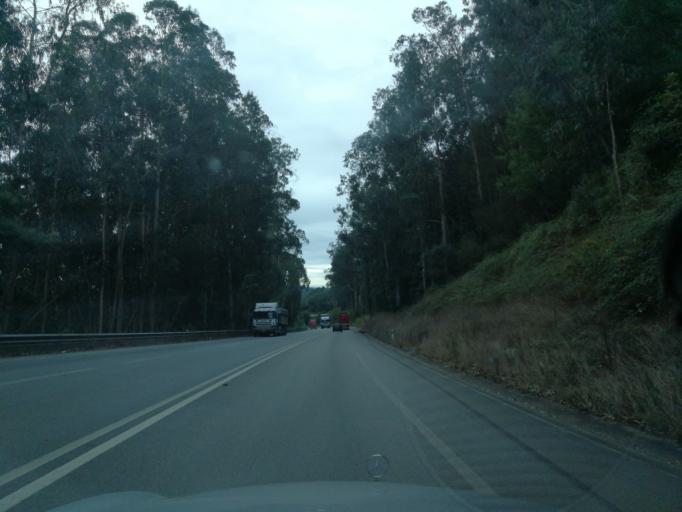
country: PT
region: Aveiro
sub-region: Agueda
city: Valongo
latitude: 40.6527
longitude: -8.4668
